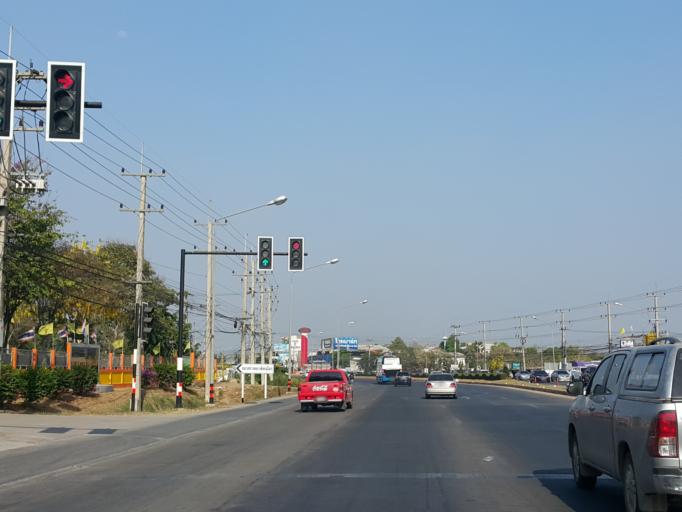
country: TH
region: Phitsanulok
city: Phitsanulok
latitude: 16.8166
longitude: 100.3027
